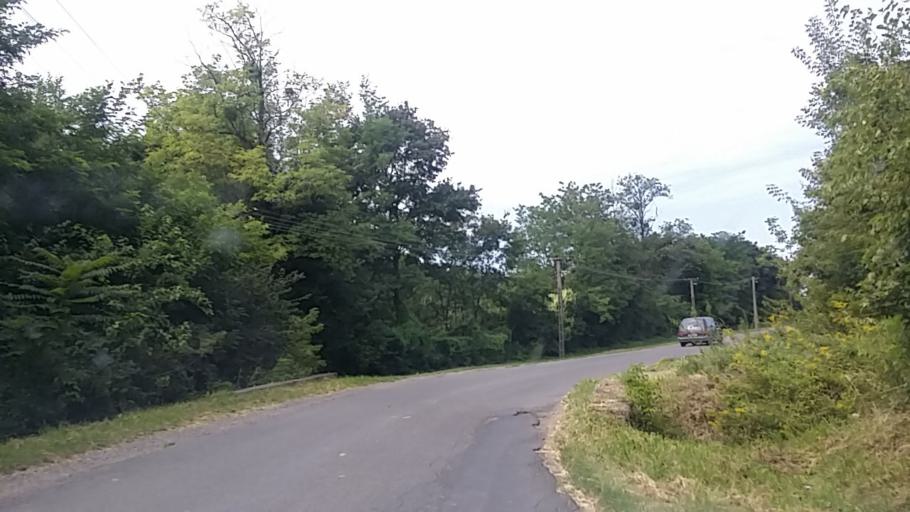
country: HU
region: Tolna
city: Dombovar
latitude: 46.3393
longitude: 18.0281
